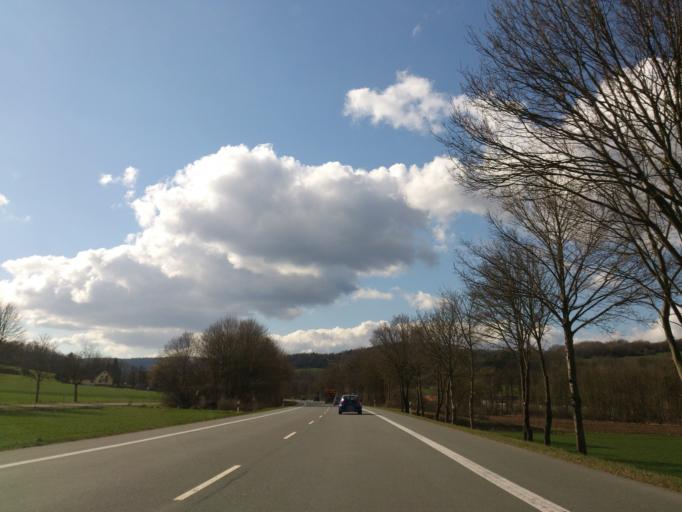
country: DE
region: North Rhine-Westphalia
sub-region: Regierungsbezirk Detmold
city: Bad Driburg
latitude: 51.7224
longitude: 9.0586
